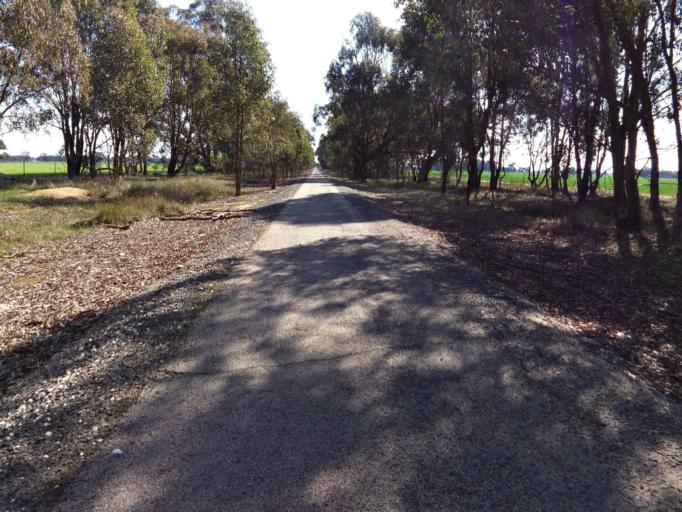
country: AU
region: New South Wales
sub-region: Corowa Shire
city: Corowa
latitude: -36.0241
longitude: 146.4288
